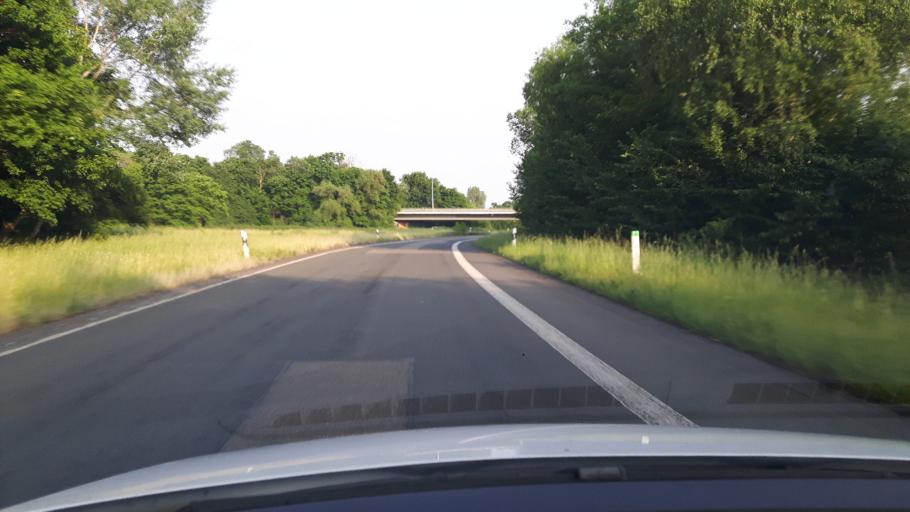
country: DE
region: North Rhine-Westphalia
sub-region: Regierungsbezirk Dusseldorf
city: Hilden
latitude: 51.1927
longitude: 6.9391
